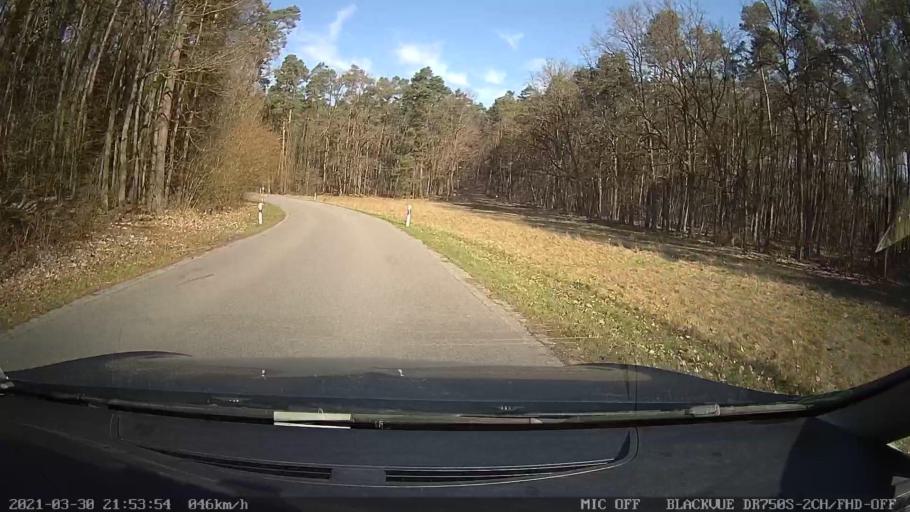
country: DE
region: Bavaria
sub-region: Upper Palatinate
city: Zeitlarn
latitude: 49.0933
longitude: 12.1184
